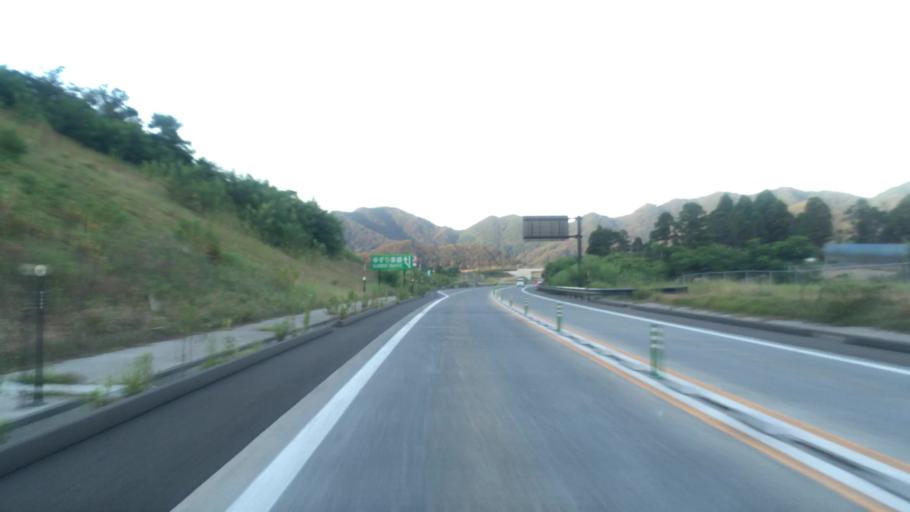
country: JP
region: Tottori
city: Tottori
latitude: 35.5491
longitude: 134.2668
